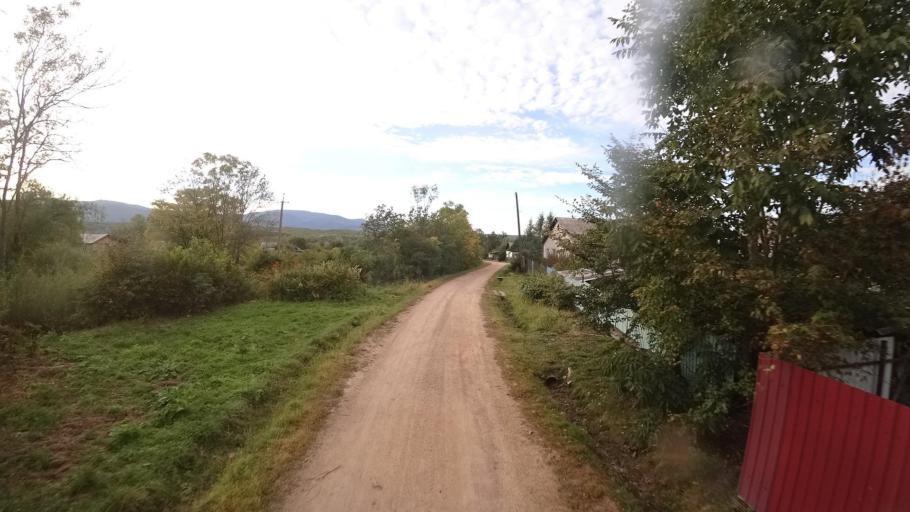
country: RU
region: Primorskiy
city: Yakovlevka
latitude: 44.4119
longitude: 133.4515
